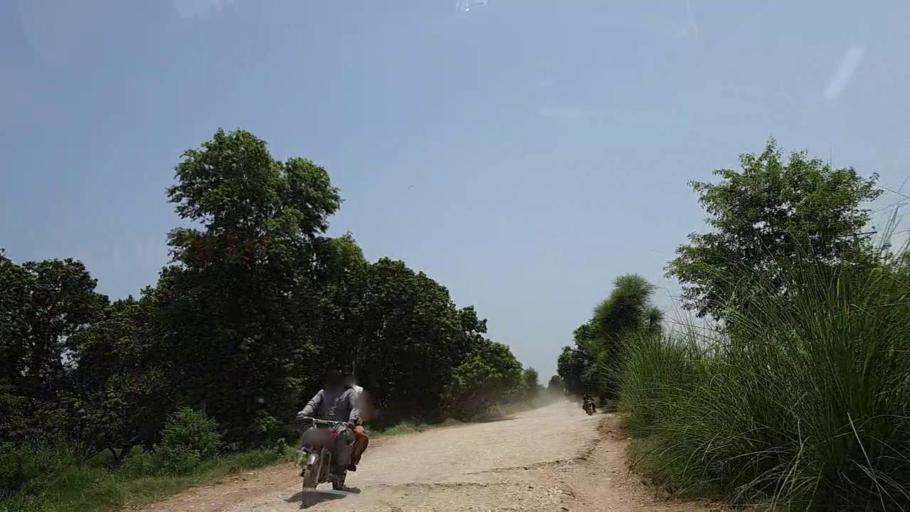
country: PK
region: Sindh
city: Tharu Shah
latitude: 26.9486
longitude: 68.0998
